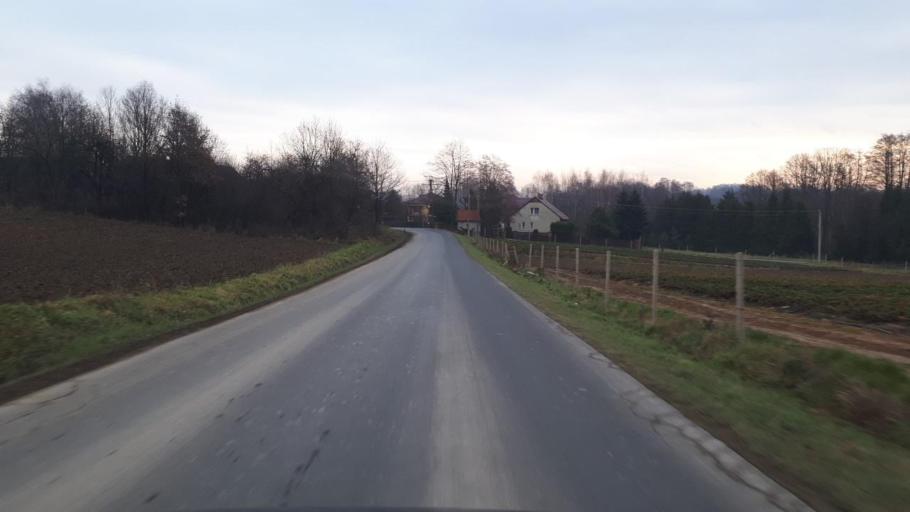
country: PL
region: Silesian Voivodeship
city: Janowice
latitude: 49.9069
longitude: 19.1011
